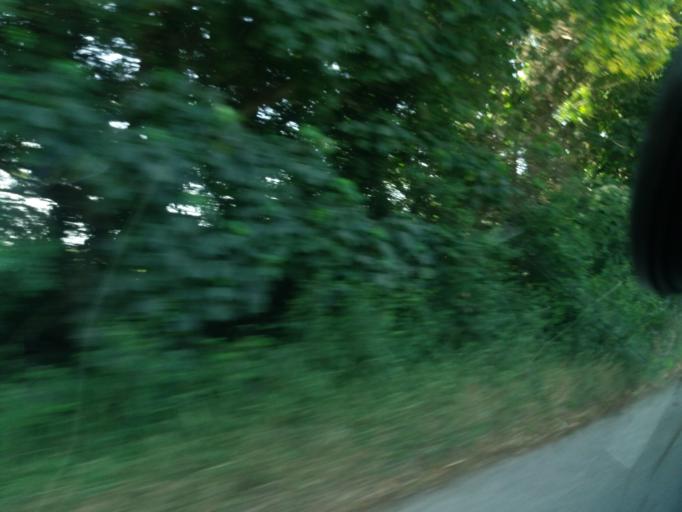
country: IE
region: Leinster
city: Lusk
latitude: 53.5214
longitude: -6.1905
